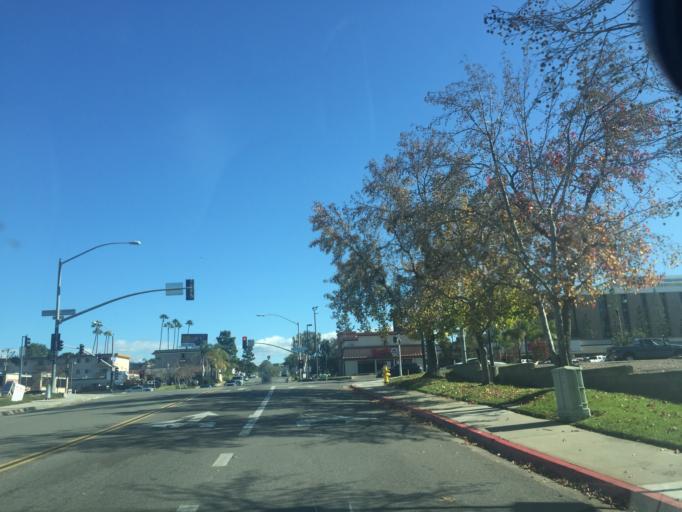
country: US
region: California
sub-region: San Diego County
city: La Mesa
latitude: 32.7929
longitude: -117.0982
